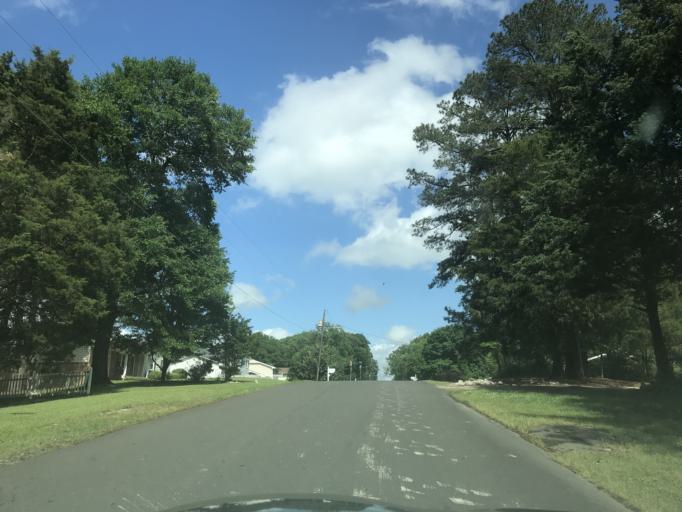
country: US
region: North Carolina
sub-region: Wake County
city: Raleigh
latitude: 35.8084
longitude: -78.5707
